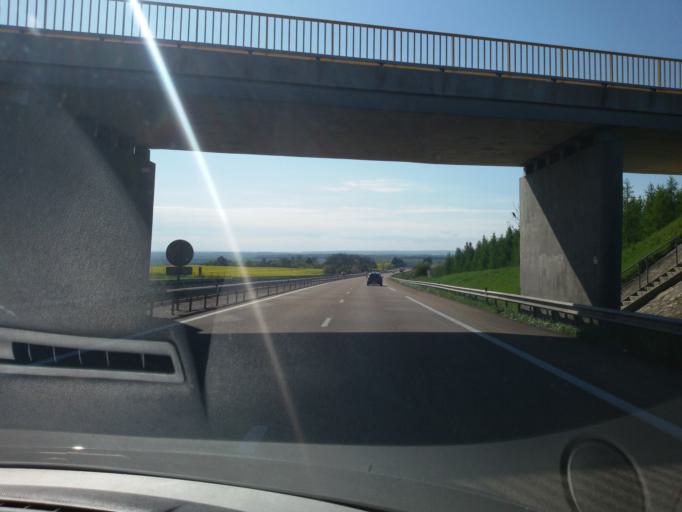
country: FR
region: Bourgogne
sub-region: Departement de l'Yonne
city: Vermenton
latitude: 47.7338
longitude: 3.7388
